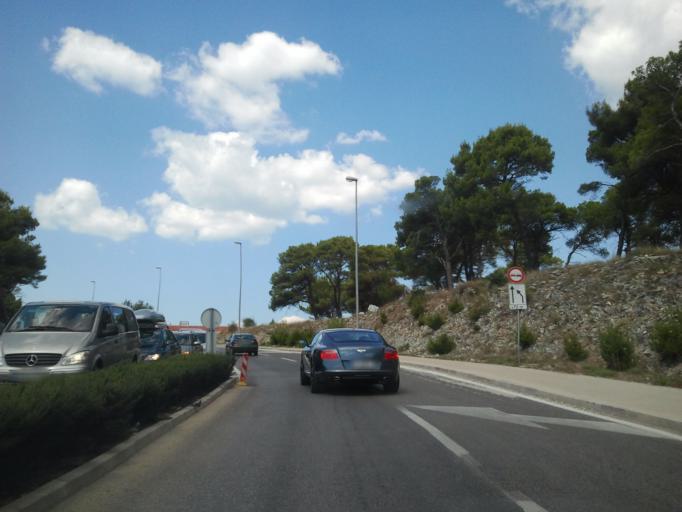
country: HR
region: Zadarska
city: Zadar
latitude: 44.1176
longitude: 15.2677
